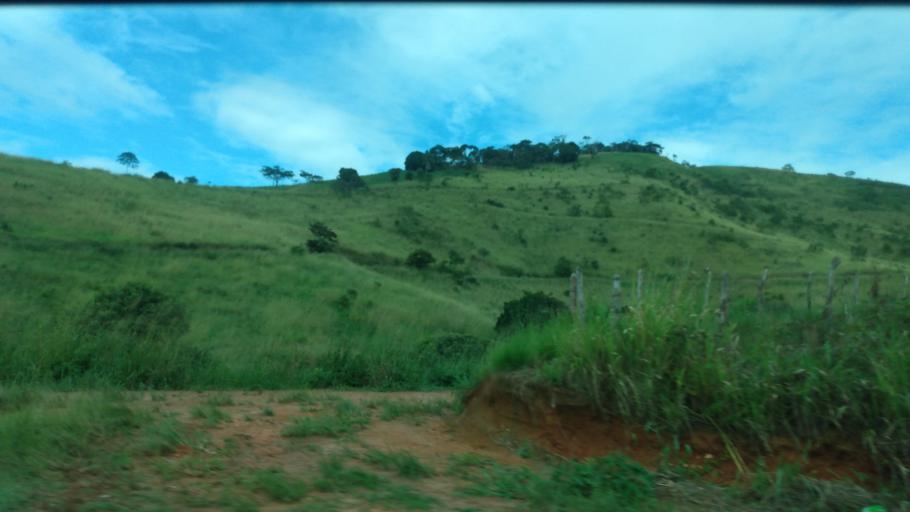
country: BR
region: Pernambuco
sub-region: Maraial
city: Maraial
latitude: -8.7236
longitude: -35.7865
